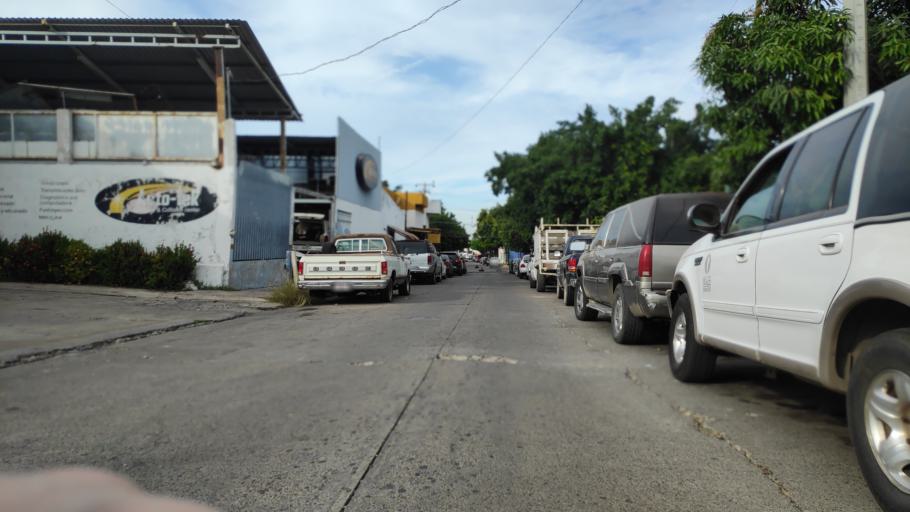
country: MX
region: Sinaloa
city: Culiacan
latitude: 24.7965
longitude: -107.3964
